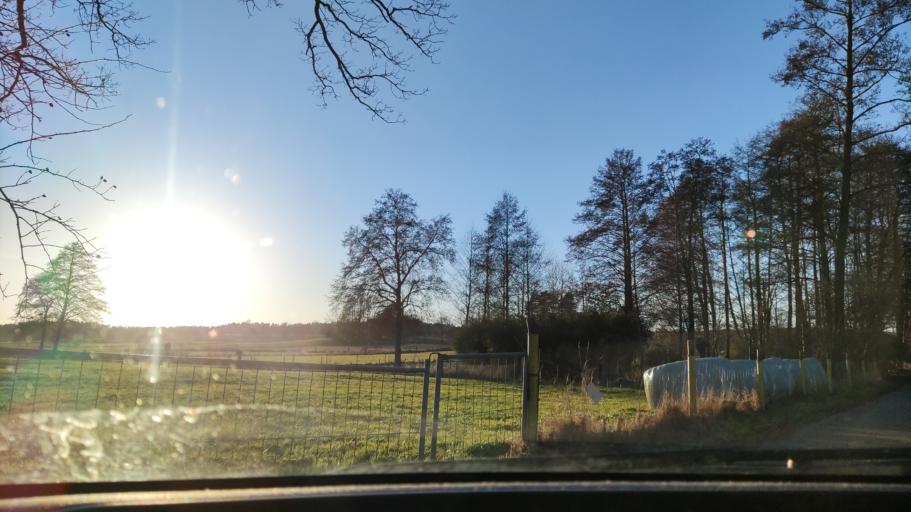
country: DE
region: Lower Saxony
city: Gohrde
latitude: 53.1546
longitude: 10.8539
